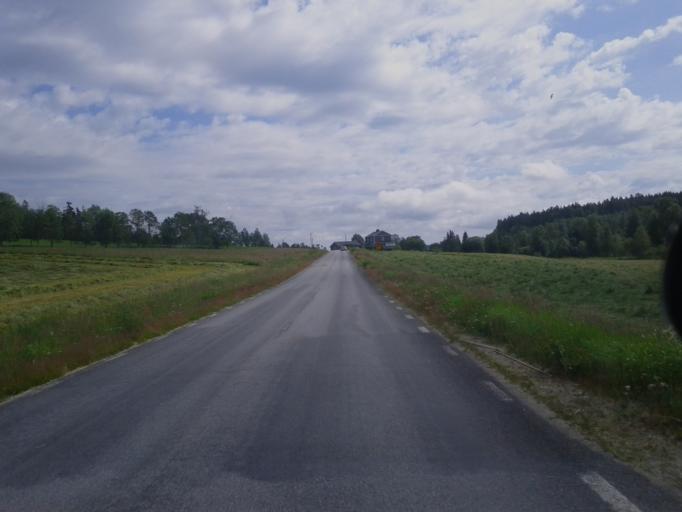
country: SE
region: Vaesternorrland
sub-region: OErnskoeldsviks Kommun
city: Ornskoldsvik
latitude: 63.2882
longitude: 18.8363
